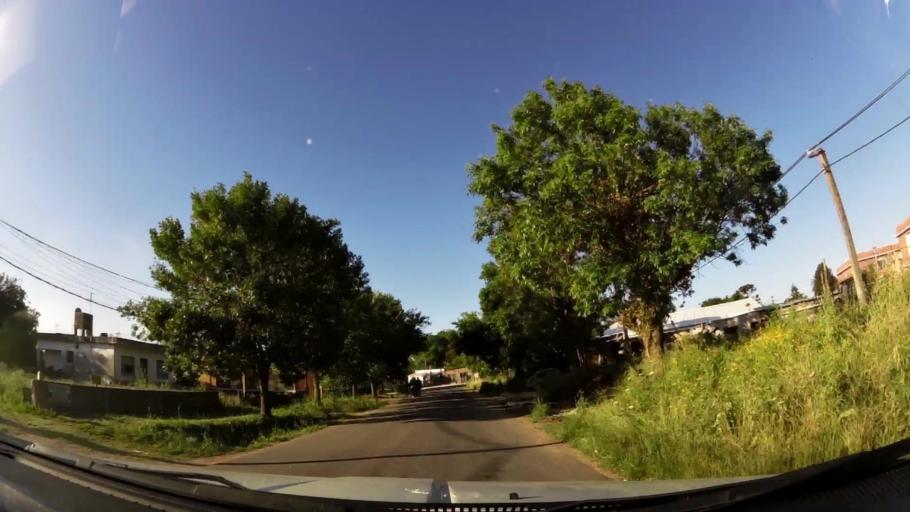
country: UY
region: Canelones
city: La Paz
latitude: -34.8331
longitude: -56.2406
